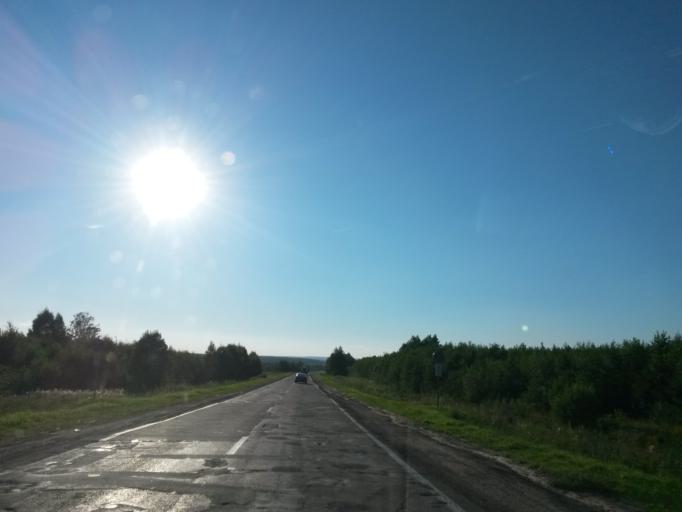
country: RU
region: Jaroslavl
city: Gavrilov-Yam
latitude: 57.2737
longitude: 39.9429
